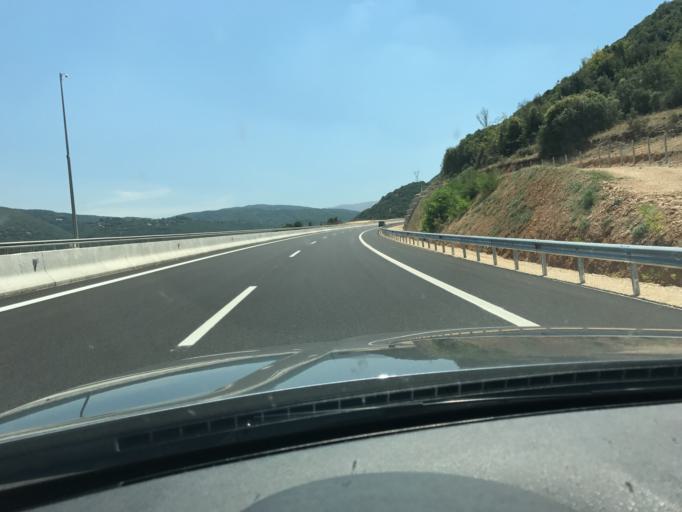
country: GR
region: Epirus
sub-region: Nomos Ioanninon
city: Agia Kyriaki
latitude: 39.5159
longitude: 20.8859
